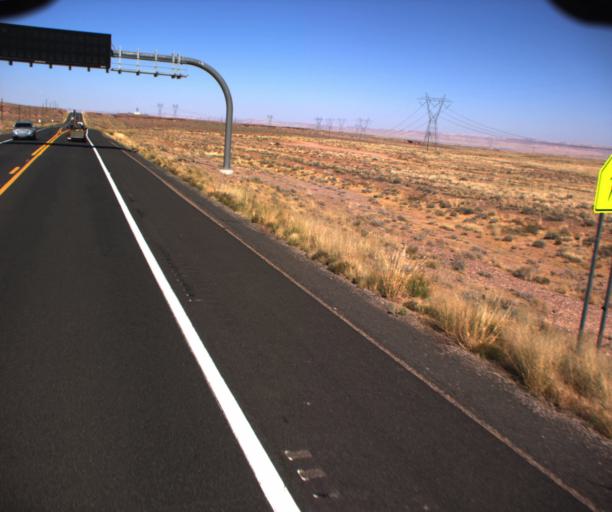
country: US
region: Arizona
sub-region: Coconino County
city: Tuba City
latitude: 35.8210
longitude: -111.4407
